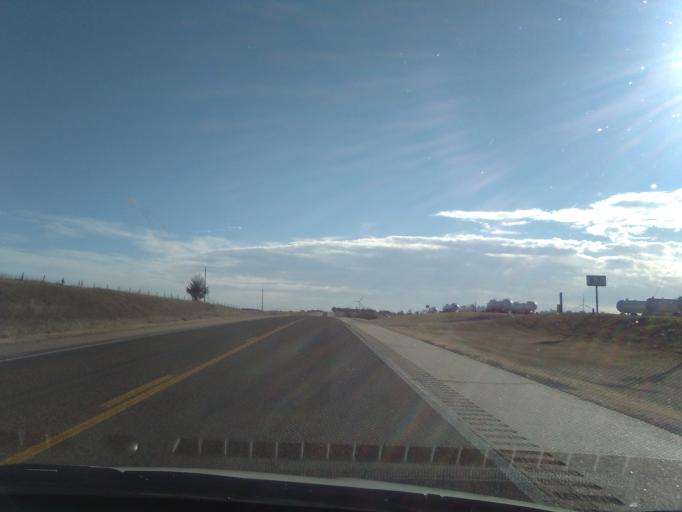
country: US
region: Nebraska
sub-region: Webster County
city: Red Cloud
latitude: 40.3207
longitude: -98.4440
